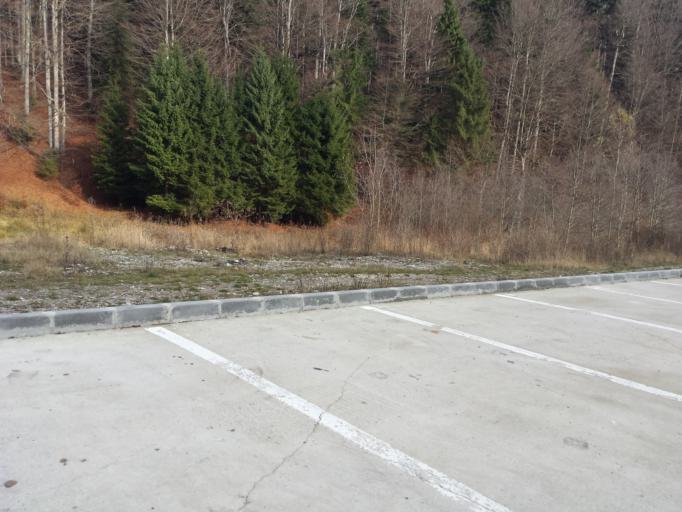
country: RO
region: Prahova
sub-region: Oras Azuga
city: Azuga
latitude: 45.4296
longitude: 25.5345
